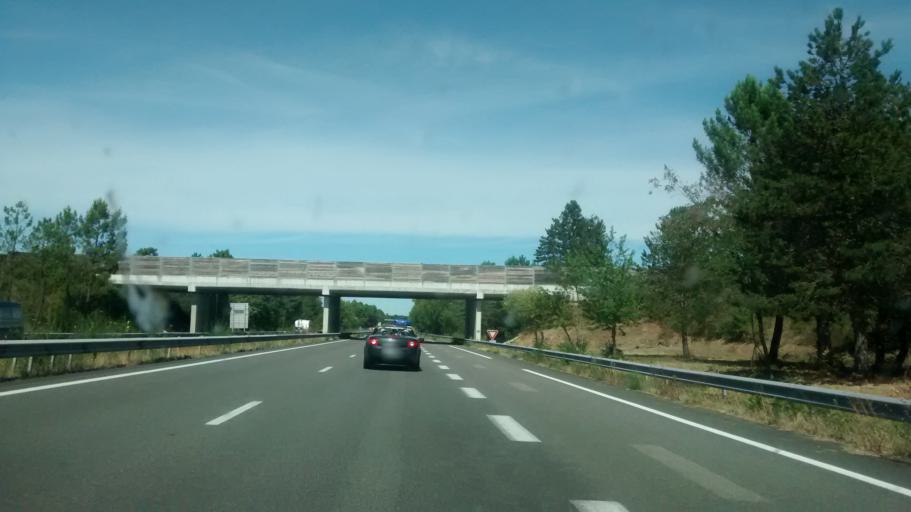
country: FR
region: Poitou-Charentes
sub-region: Departement de la Charente-Maritime
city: Saint-Genis-de-Saintonge
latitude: 45.4462
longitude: -0.6101
